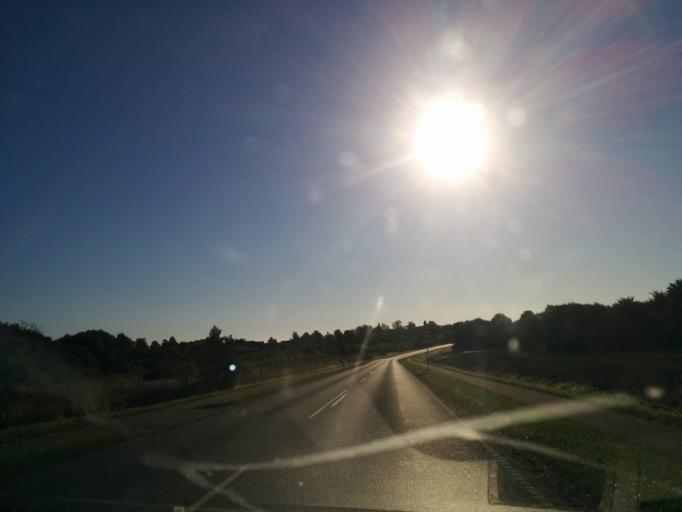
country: DK
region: South Denmark
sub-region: Kolding Kommune
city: Sonder Bjert
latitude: 55.4579
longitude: 9.5481
